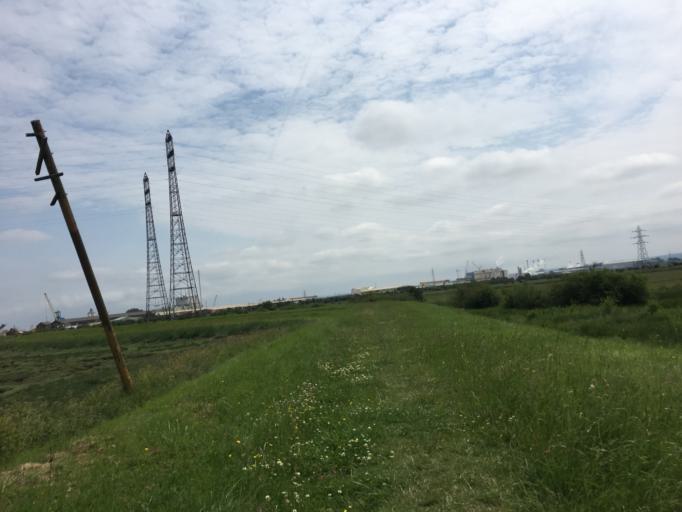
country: GB
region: England
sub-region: Kent
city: Queenborough
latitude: 51.3881
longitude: 0.7503
